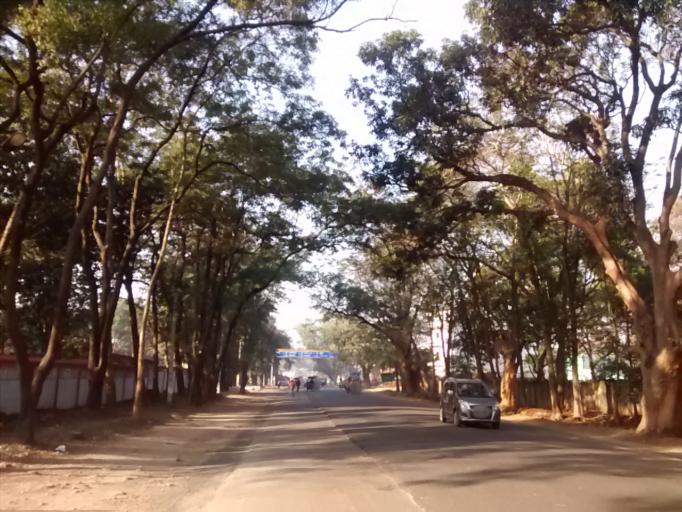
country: IN
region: Jharkhand
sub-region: Ranchi
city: Ranchi
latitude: 23.3901
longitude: 85.3780
